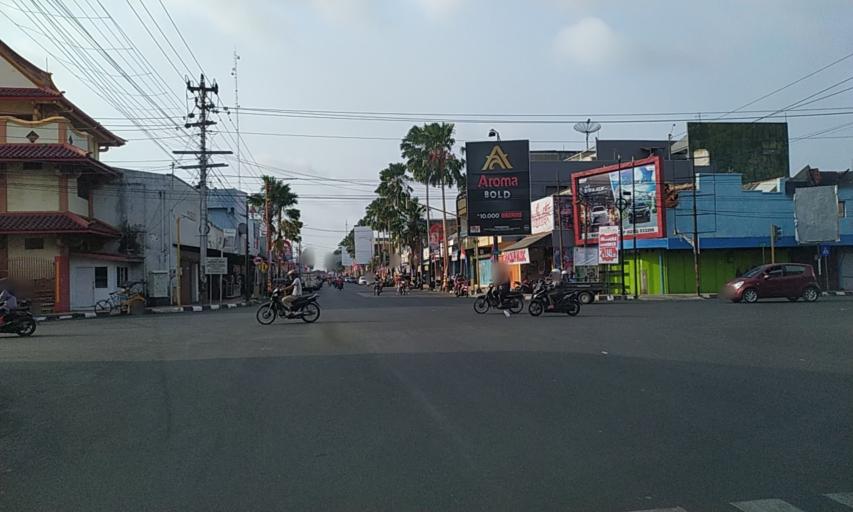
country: ID
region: Central Java
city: Karangbadar Kidul
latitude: -7.7332
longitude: 109.0095
